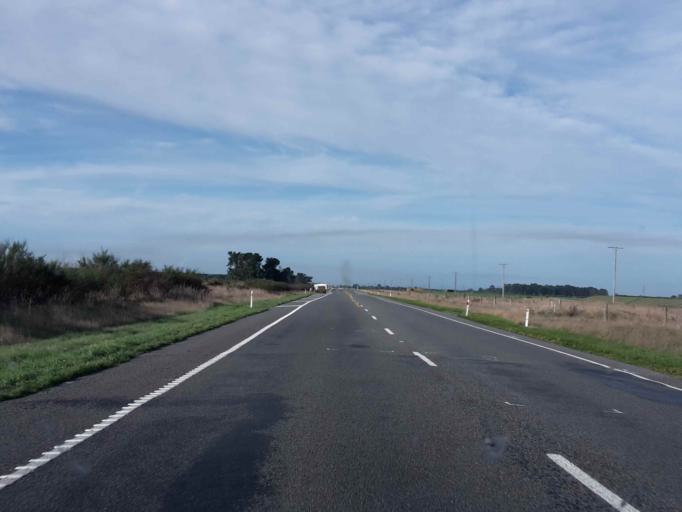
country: NZ
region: Canterbury
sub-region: Ashburton District
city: Tinwald
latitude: -44.0234
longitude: 171.5043
